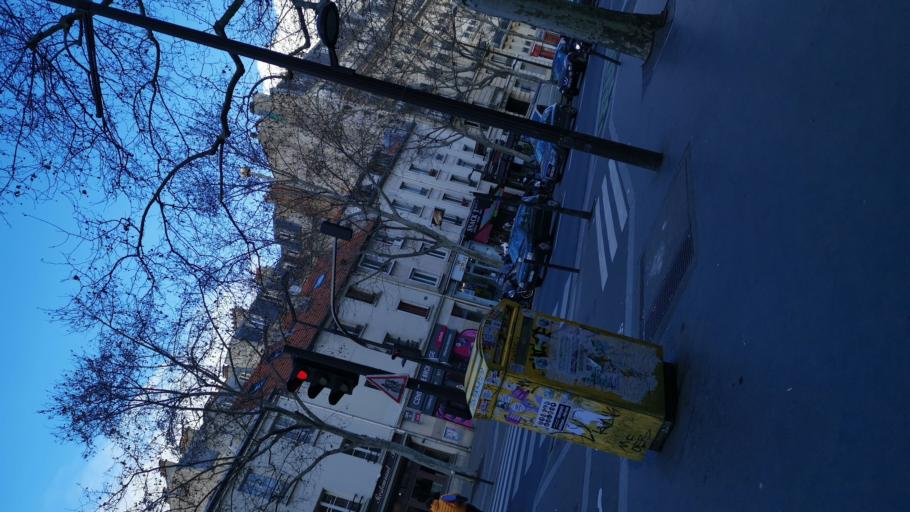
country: FR
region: Ile-de-France
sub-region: Departement de Seine-Saint-Denis
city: Le Pre-Saint-Gervais
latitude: 48.8871
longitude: 2.3869
